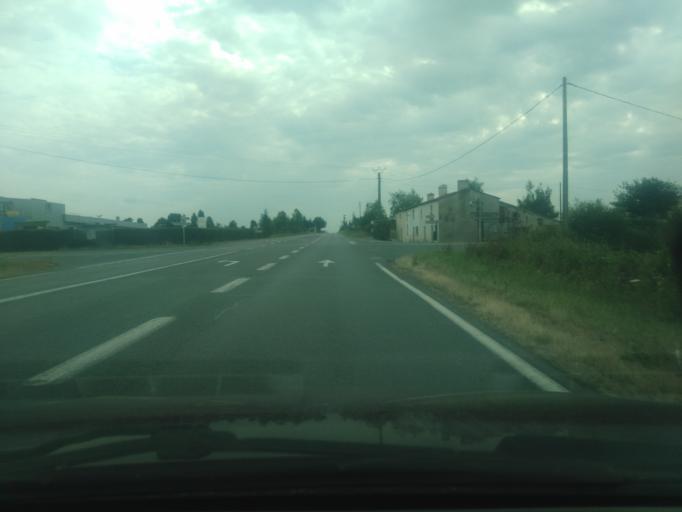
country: FR
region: Pays de la Loire
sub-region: Departement de la Vendee
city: Les Essarts
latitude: 46.7435
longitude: -1.2698
